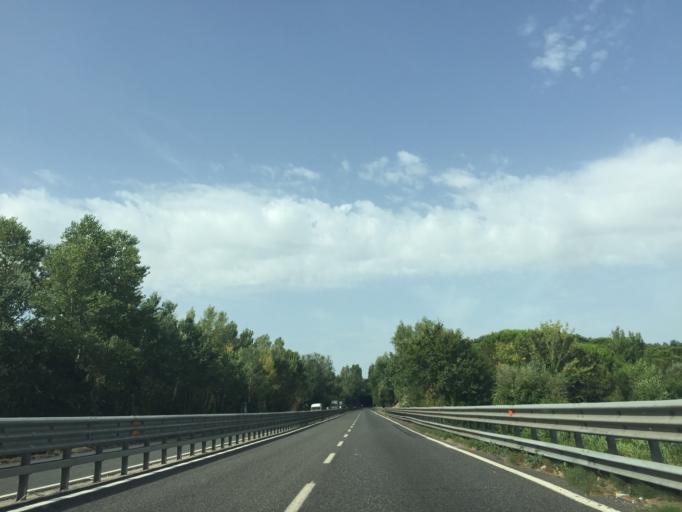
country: IT
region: Tuscany
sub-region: Province of Pisa
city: San Miniato
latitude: 43.6889
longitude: 10.7800
